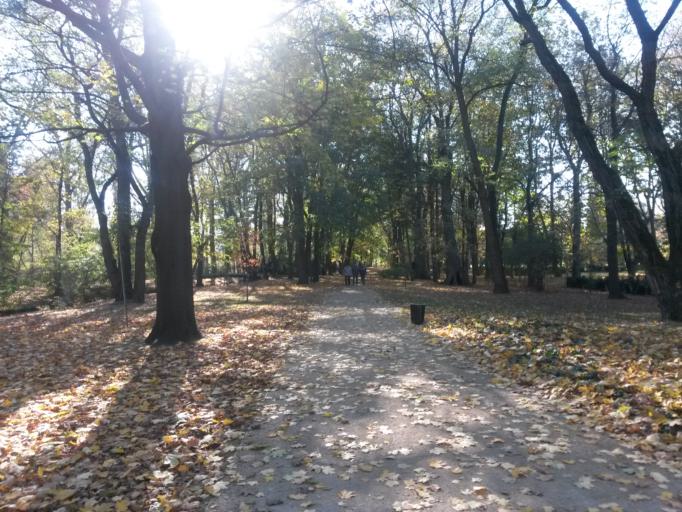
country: PL
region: Masovian Voivodeship
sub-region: Warszawa
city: Mokotow
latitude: 52.2095
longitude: 21.0347
